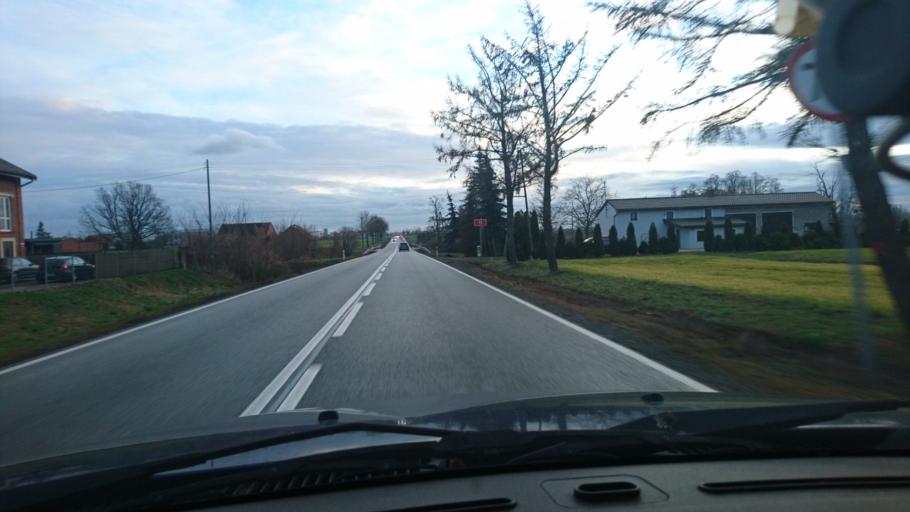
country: PL
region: Opole Voivodeship
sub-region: Powiat kluczborski
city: Kluczbork
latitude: 51.0078
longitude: 18.2046
